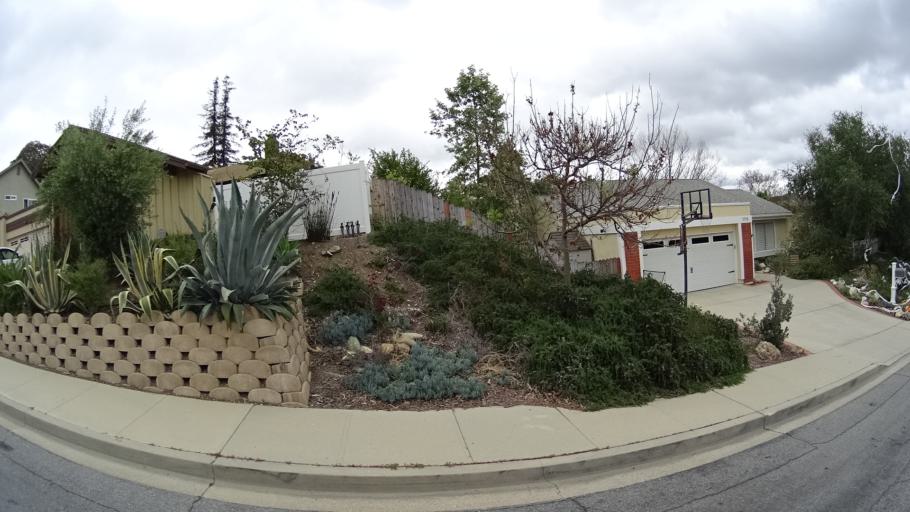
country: US
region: California
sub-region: Ventura County
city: Casa Conejo
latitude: 34.2212
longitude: -118.8996
